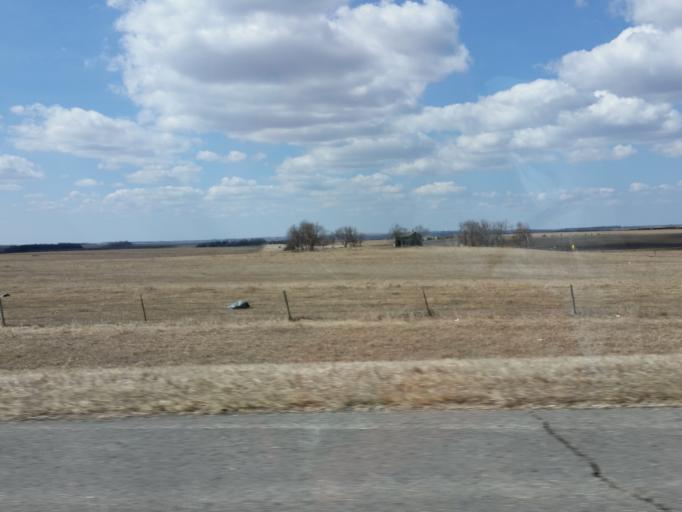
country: US
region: South Dakota
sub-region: Codington County
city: Watertown
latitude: 45.1937
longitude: -97.0567
